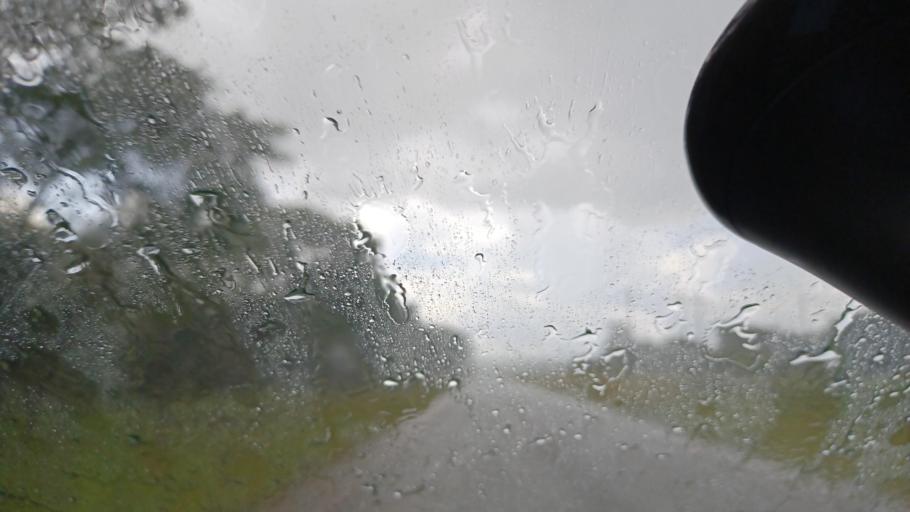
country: ZM
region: North-Western
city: Kasempa
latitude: -13.0977
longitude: 25.9056
